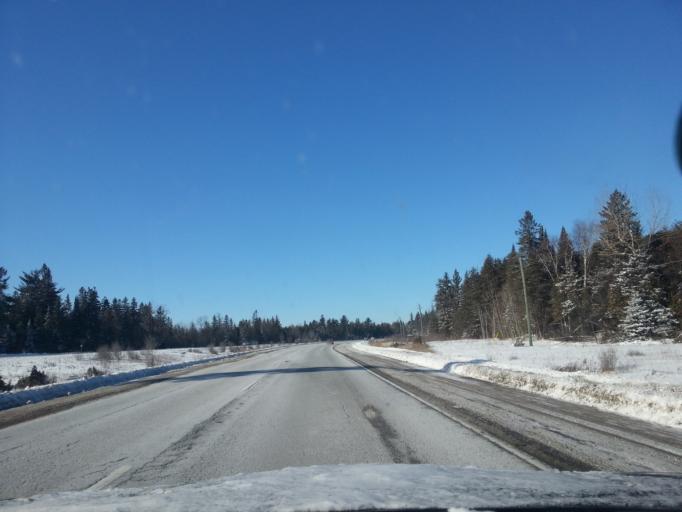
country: CA
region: Ontario
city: Bells Corners
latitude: 45.2727
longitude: -75.9840
